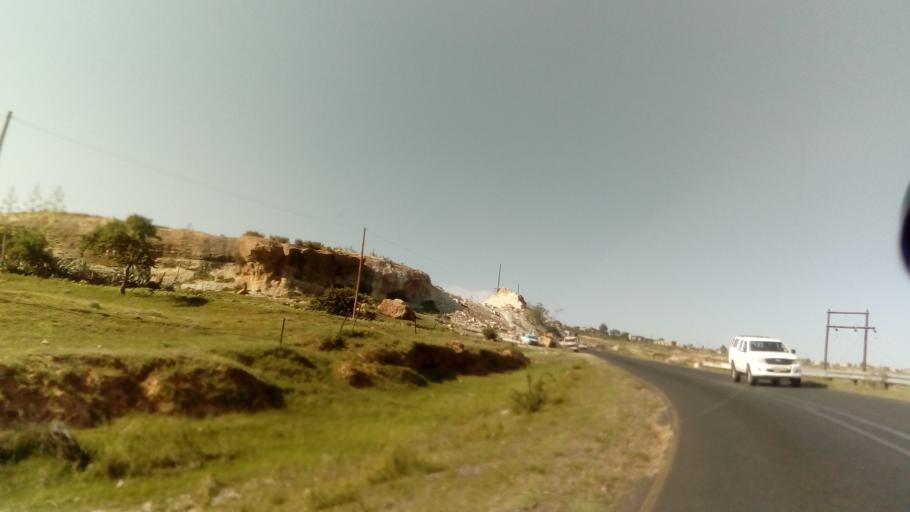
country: LS
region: Berea
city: Teyateyaneng
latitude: -29.1445
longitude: 27.6994
